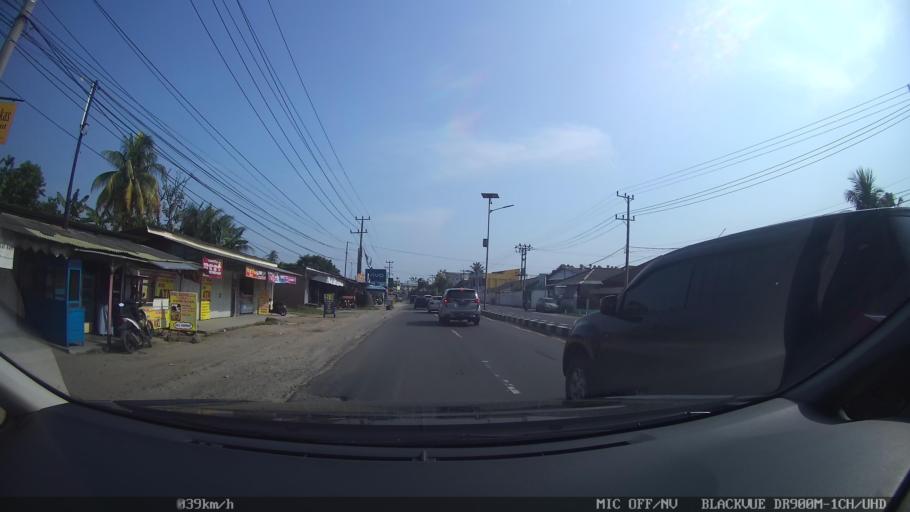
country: ID
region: Lampung
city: Natar
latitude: -5.2860
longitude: 105.1909
